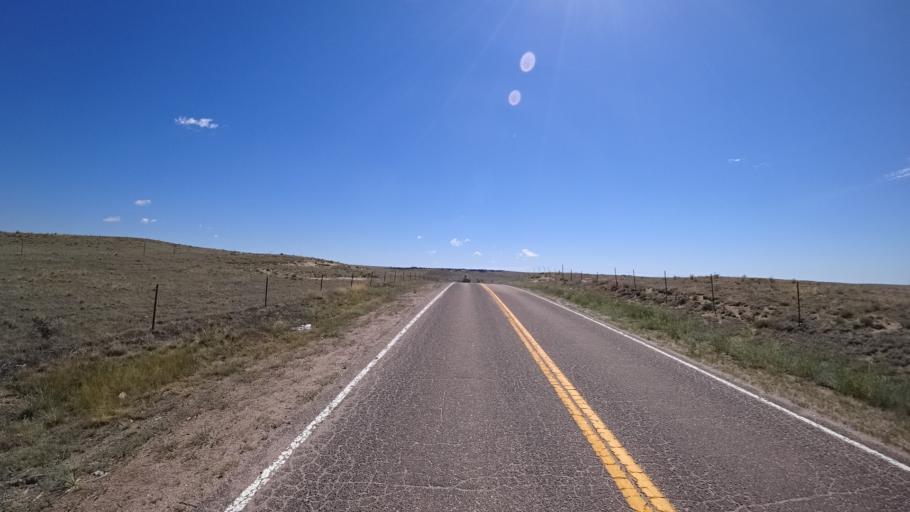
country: US
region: Colorado
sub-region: El Paso County
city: Security-Widefield
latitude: 38.7810
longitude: -104.6219
